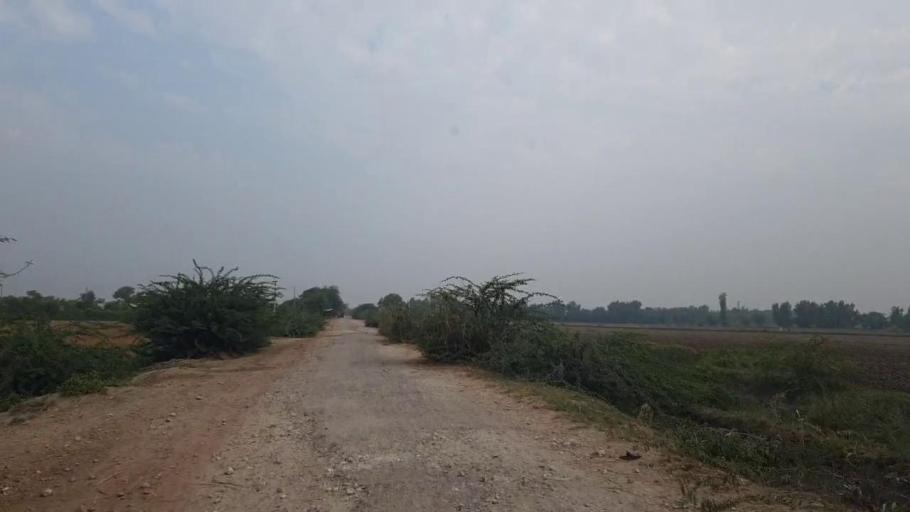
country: PK
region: Sindh
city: Talhar
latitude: 24.8248
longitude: 68.8789
